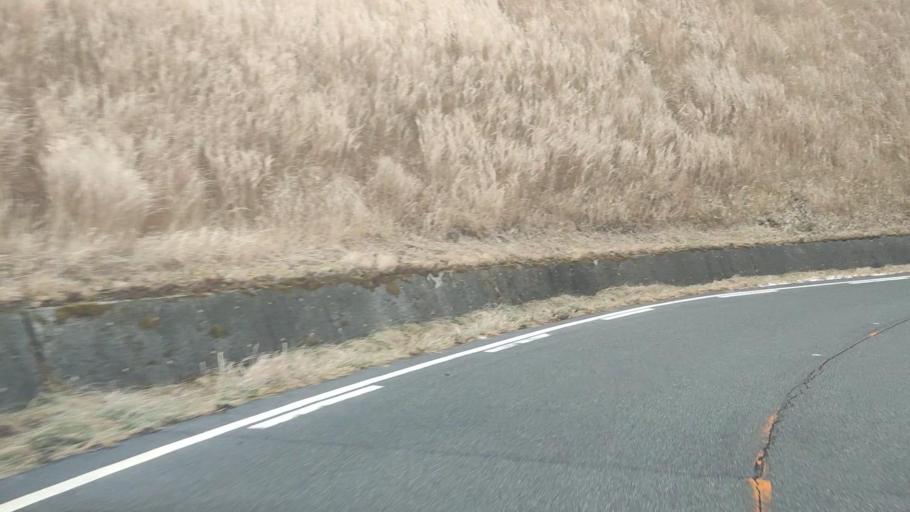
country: JP
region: Kumamoto
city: Aso
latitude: 32.9050
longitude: 131.1541
